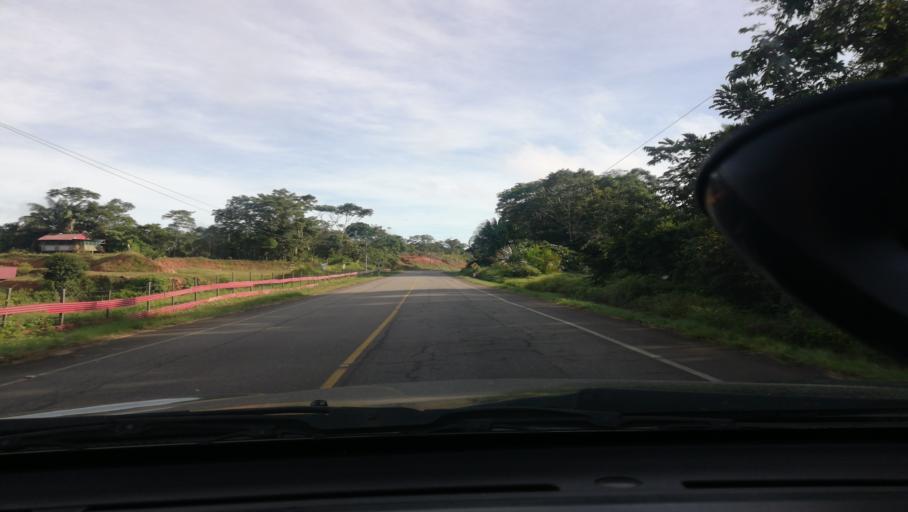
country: PE
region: Loreto
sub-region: Provincia de Loreto
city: Nauta
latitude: -4.4158
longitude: -73.5840
